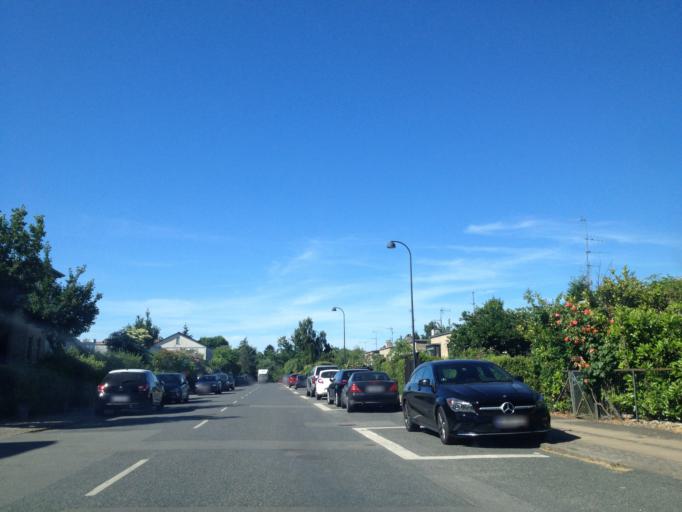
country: DK
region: Capital Region
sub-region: Gentofte Kommune
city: Charlottenlund
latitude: 55.7644
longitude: 12.5863
